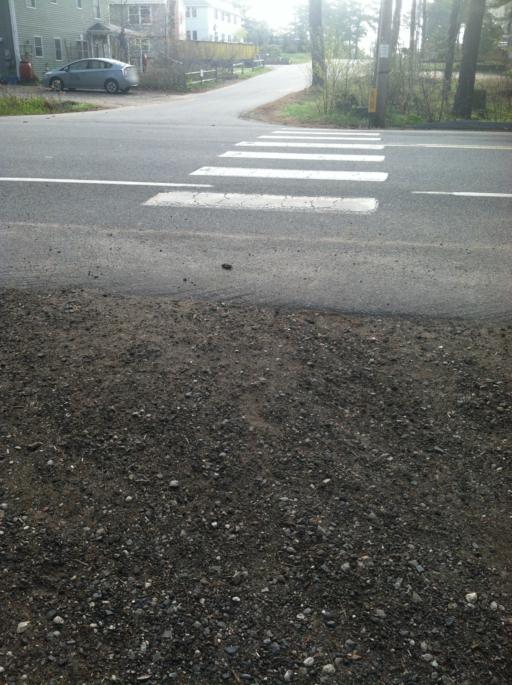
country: US
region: Maine
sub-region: York County
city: Old Orchard Beach
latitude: 43.4718
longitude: -70.3864
